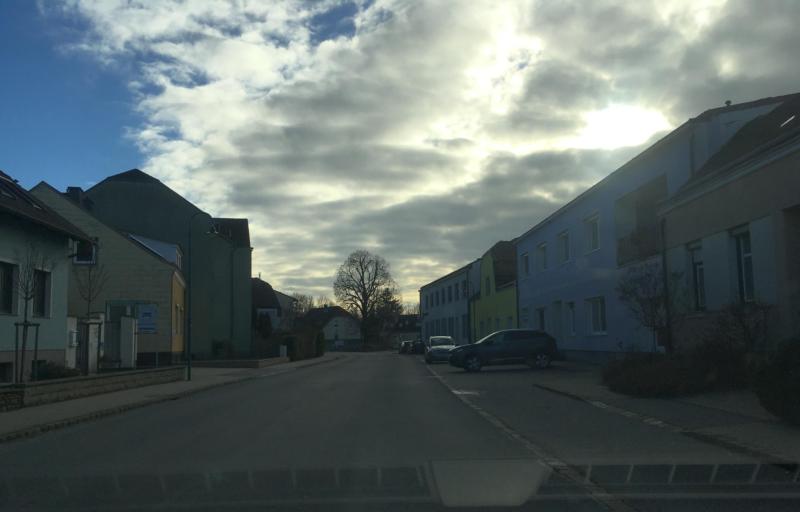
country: AT
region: Lower Austria
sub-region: Politischer Bezirk Ganserndorf
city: Eckartsau
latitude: 48.1459
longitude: 16.7967
